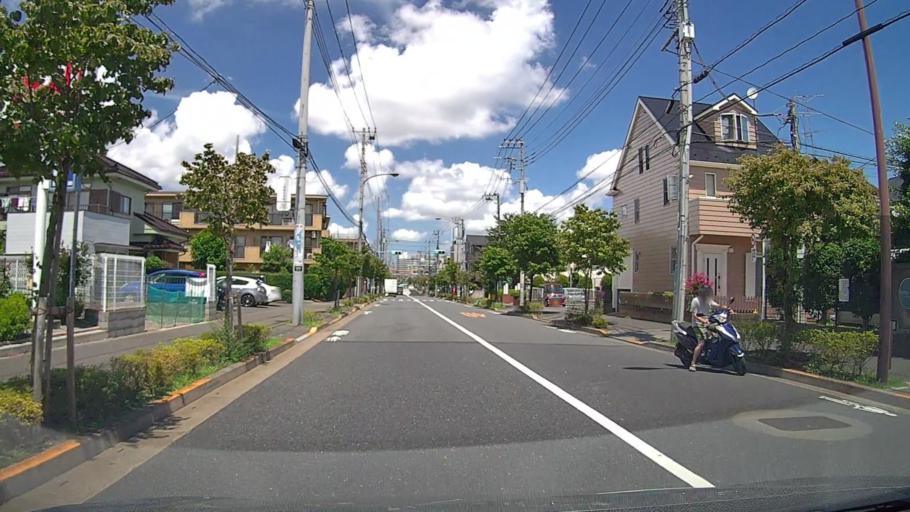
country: JP
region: Tokyo
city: Nishi-Tokyo-shi
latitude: 35.7339
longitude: 139.5432
